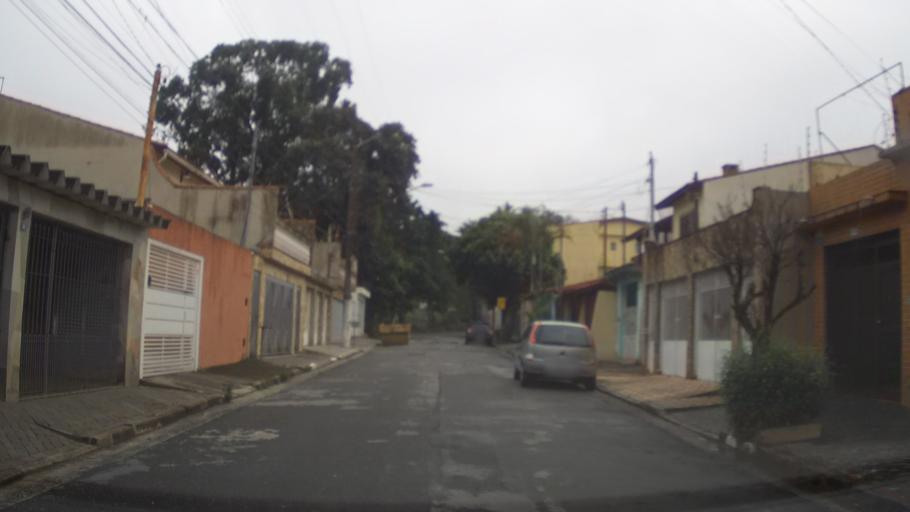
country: BR
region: Sao Paulo
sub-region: Guarulhos
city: Guarulhos
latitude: -23.4984
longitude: -46.5569
